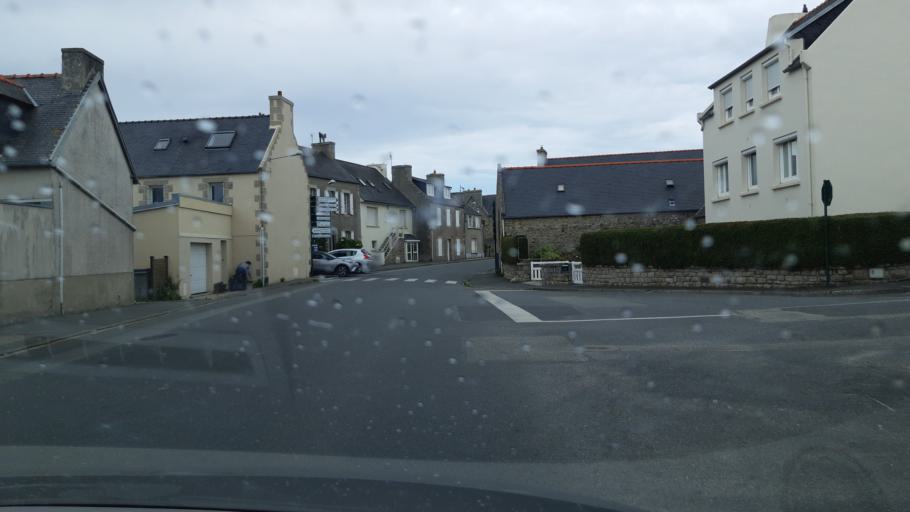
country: FR
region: Brittany
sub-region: Departement du Finistere
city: Roscoff
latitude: 48.7172
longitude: -3.9848
